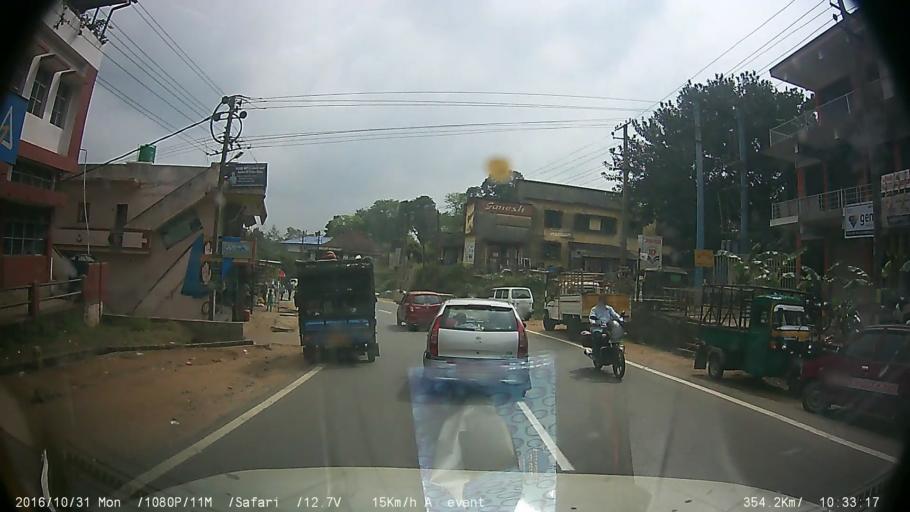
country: IN
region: Karnataka
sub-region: Kodagu
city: Suntikoppa
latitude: 12.4527
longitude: 75.8317
